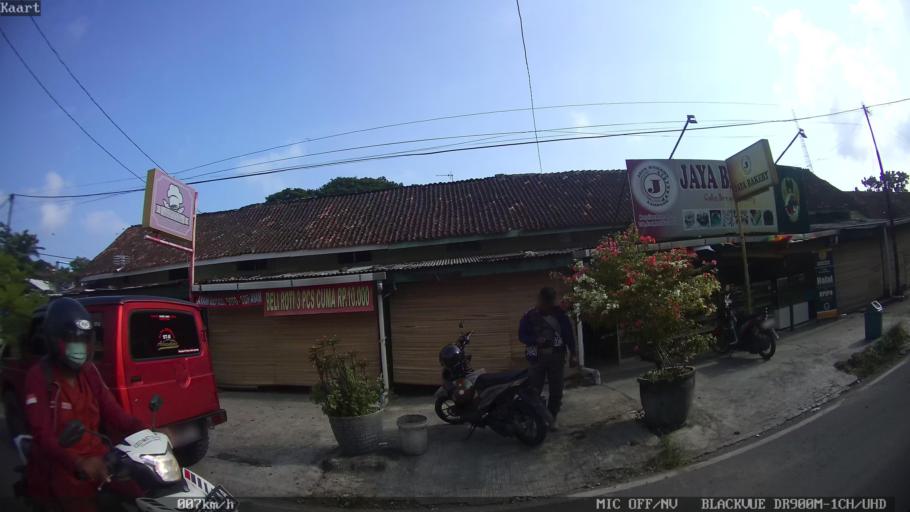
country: ID
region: Lampung
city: Kedaton
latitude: -5.4028
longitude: 105.2589
